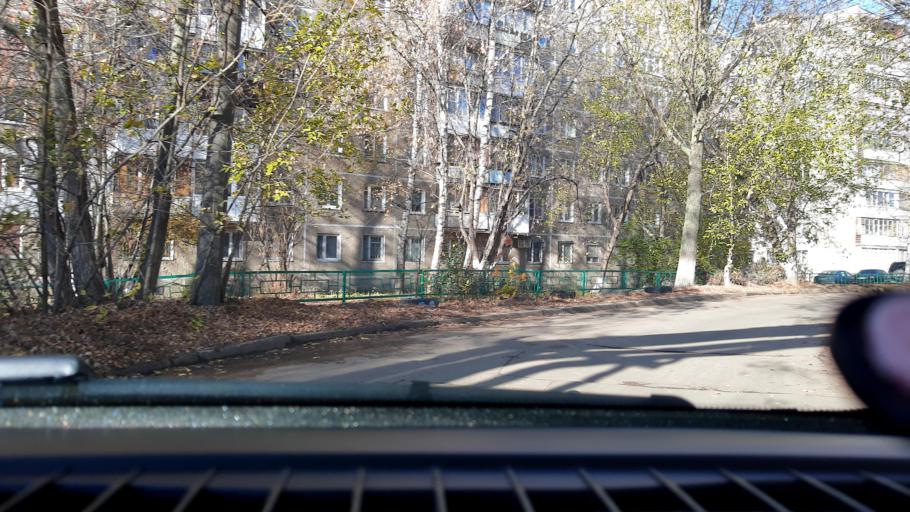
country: RU
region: Nizjnij Novgorod
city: Nizhniy Novgorod
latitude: 56.2857
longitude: 43.9485
